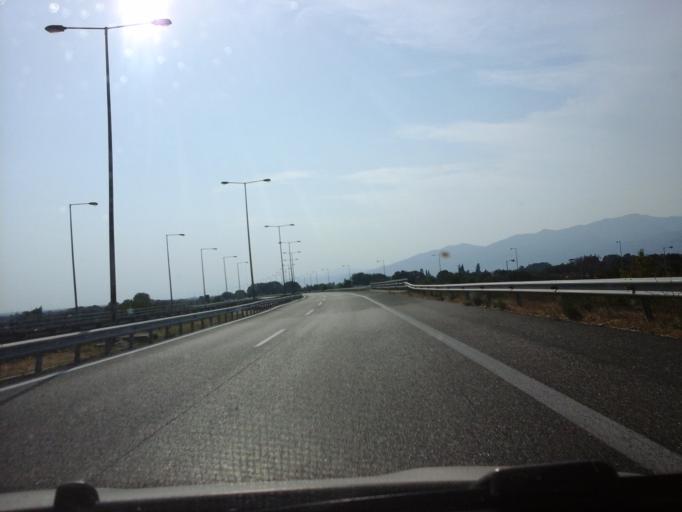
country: GR
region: East Macedonia and Thrace
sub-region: Nomos Rodopis
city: Komotini
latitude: 41.0963
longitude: 25.4337
